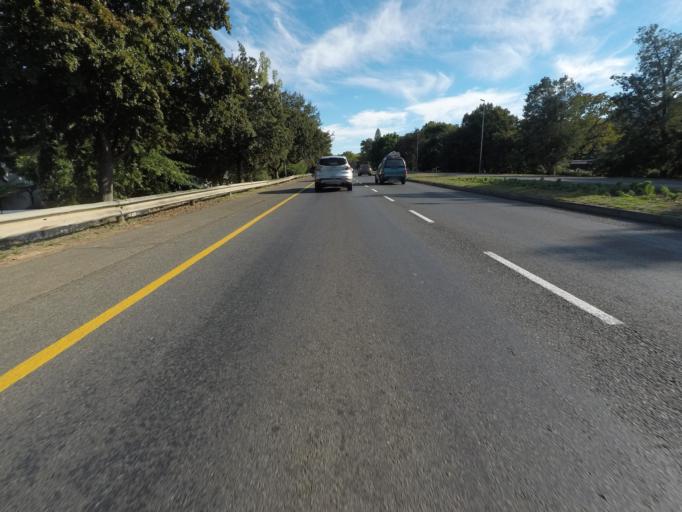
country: ZA
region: Western Cape
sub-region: Cape Winelands District Municipality
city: Stellenbosch
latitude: -33.9426
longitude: 18.8521
